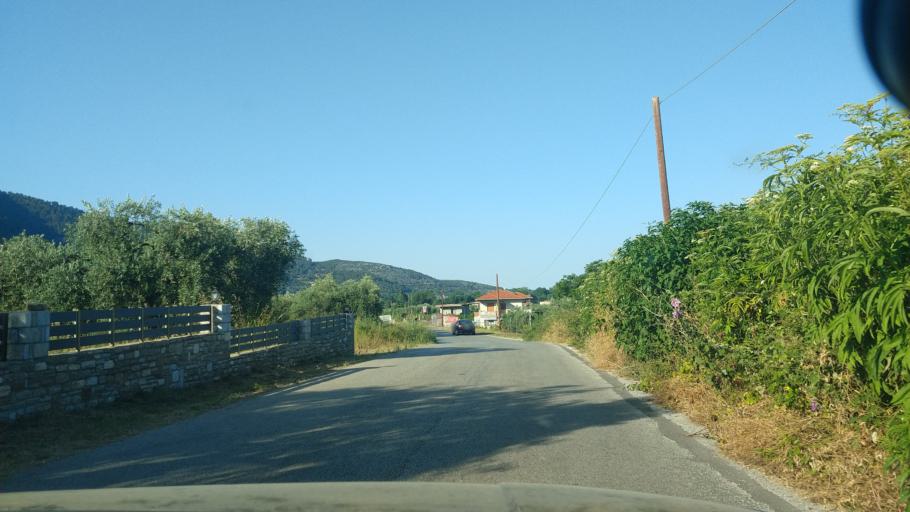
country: GR
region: East Macedonia and Thrace
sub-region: Nomos Kavalas
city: Potamia
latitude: 40.7164
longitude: 24.7456
